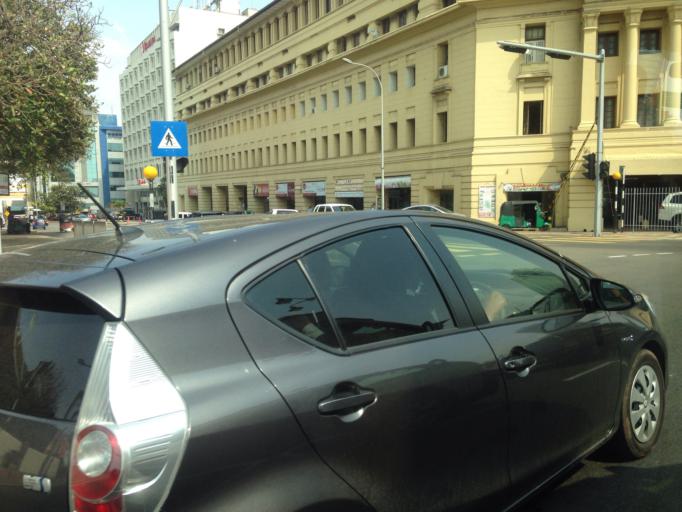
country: LK
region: Western
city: Colombo
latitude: 6.9212
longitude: 79.8465
